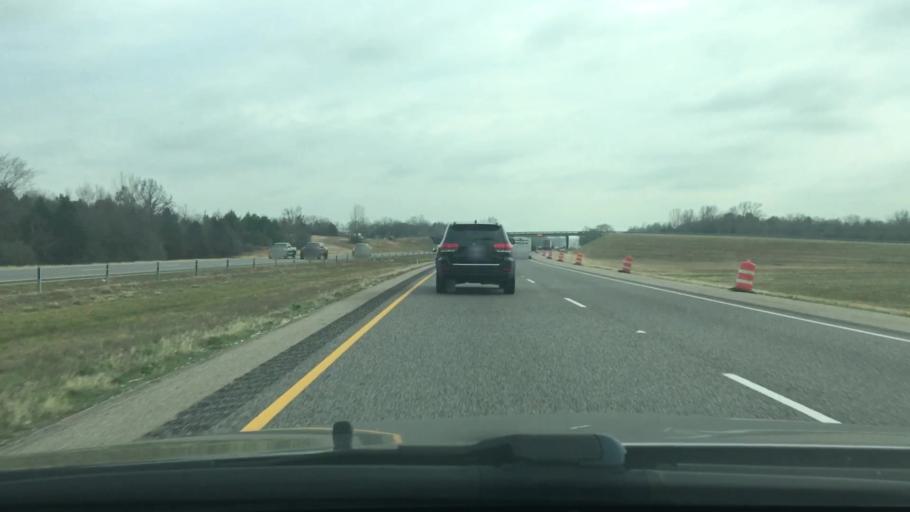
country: US
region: Texas
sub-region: Leon County
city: Buffalo
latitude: 31.5028
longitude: -96.0983
